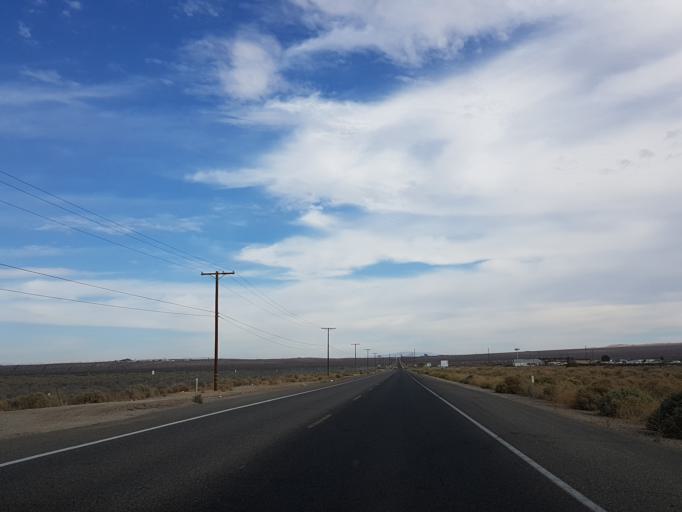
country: US
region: California
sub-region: Kern County
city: Ridgecrest
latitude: 35.6225
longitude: -117.6419
